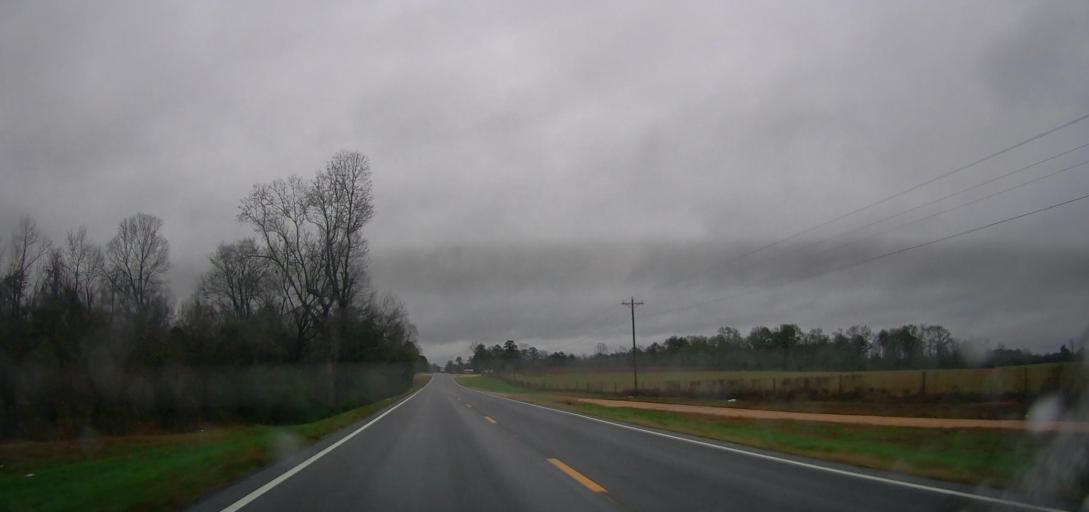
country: US
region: Alabama
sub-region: Chilton County
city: Jemison
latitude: 32.8070
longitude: -86.9225
